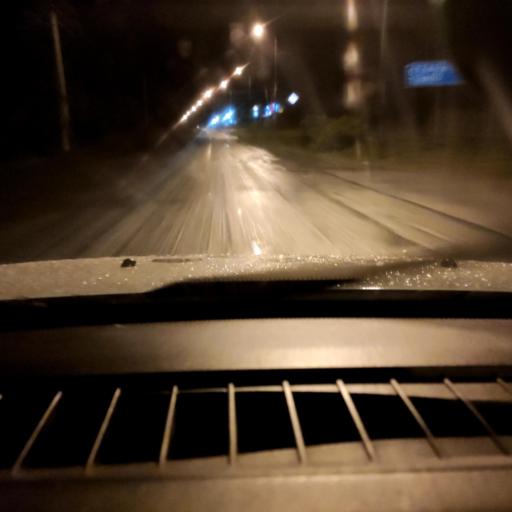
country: RU
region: Udmurtiya
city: Khokhryaki
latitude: 57.1925
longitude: 53.1543
